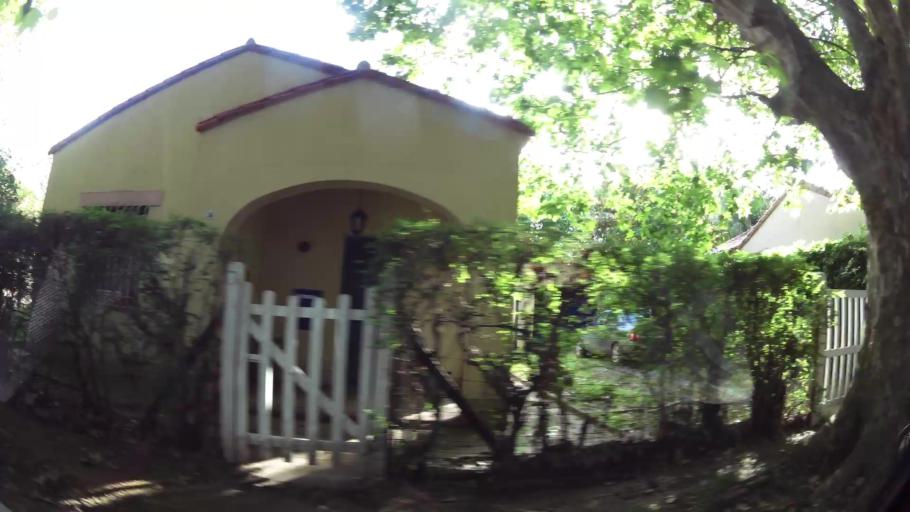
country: AR
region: Buenos Aires
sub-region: Partido de Quilmes
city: Quilmes
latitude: -34.7354
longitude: -58.2568
